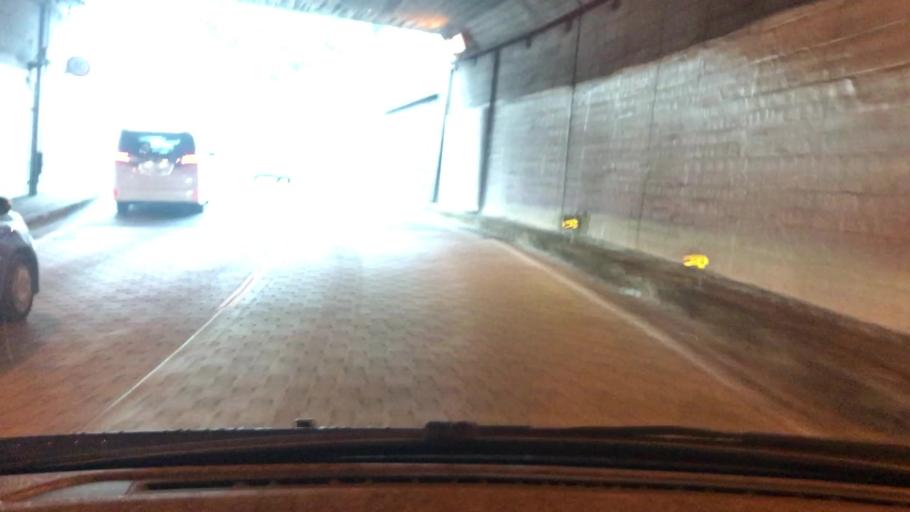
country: JP
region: Hyogo
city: Kobe
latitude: 34.7049
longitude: 135.1964
